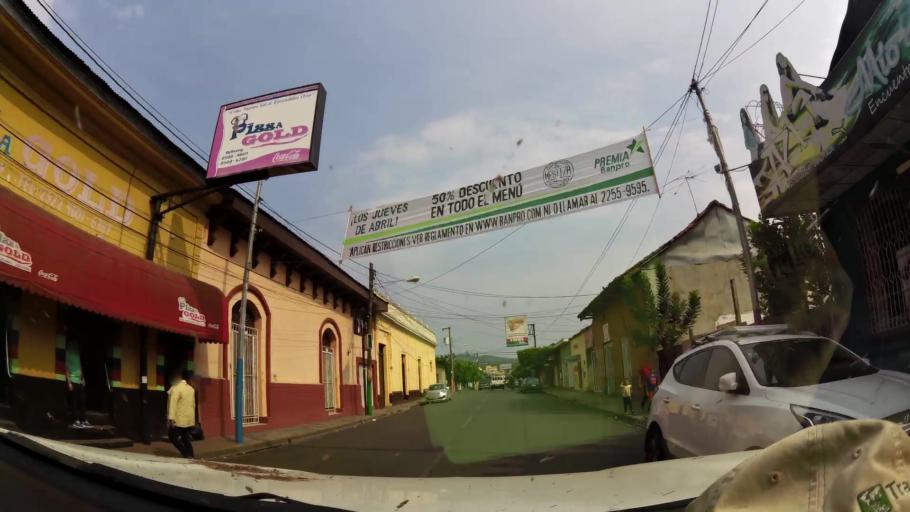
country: NI
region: Masaya
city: Masaya
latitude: 11.9728
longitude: -86.0957
